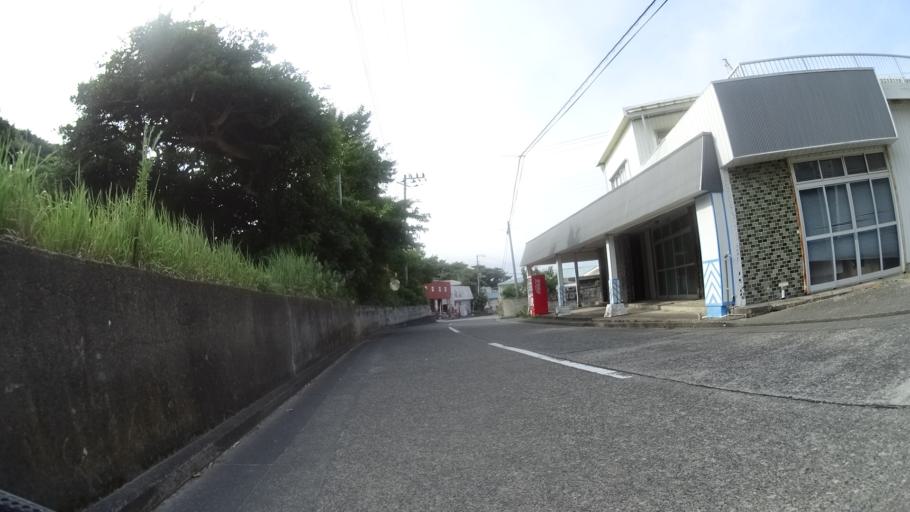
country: JP
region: Shizuoka
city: Shimoda
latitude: 34.3286
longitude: 139.2153
